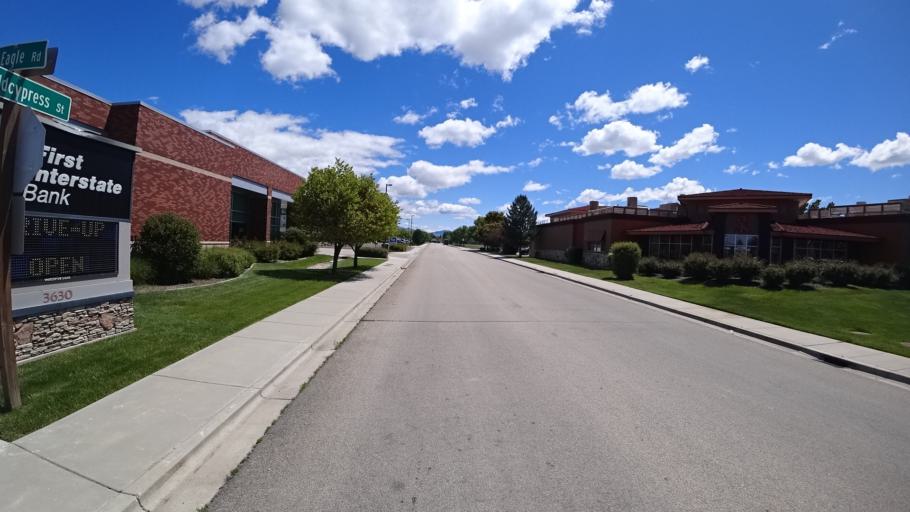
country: US
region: Idaho
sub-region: Ada County
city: Meridian
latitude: 43.6376
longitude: -116.3540
